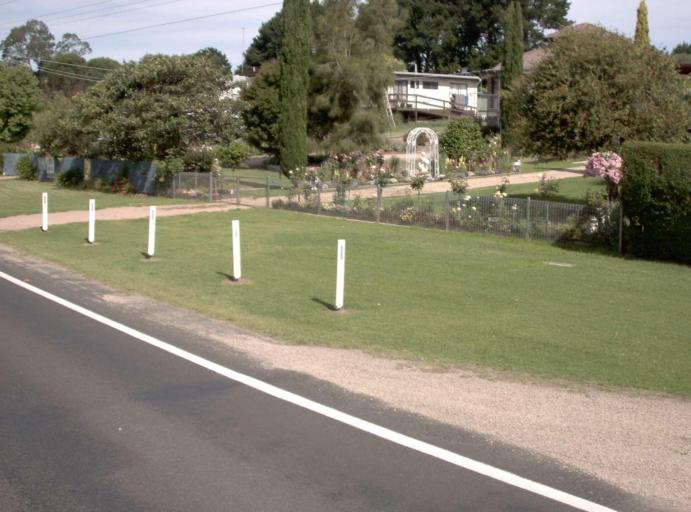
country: AU
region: Victoria
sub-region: East Gippsland
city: Lakes Entrance
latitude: -37.8219
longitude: 147.8645
